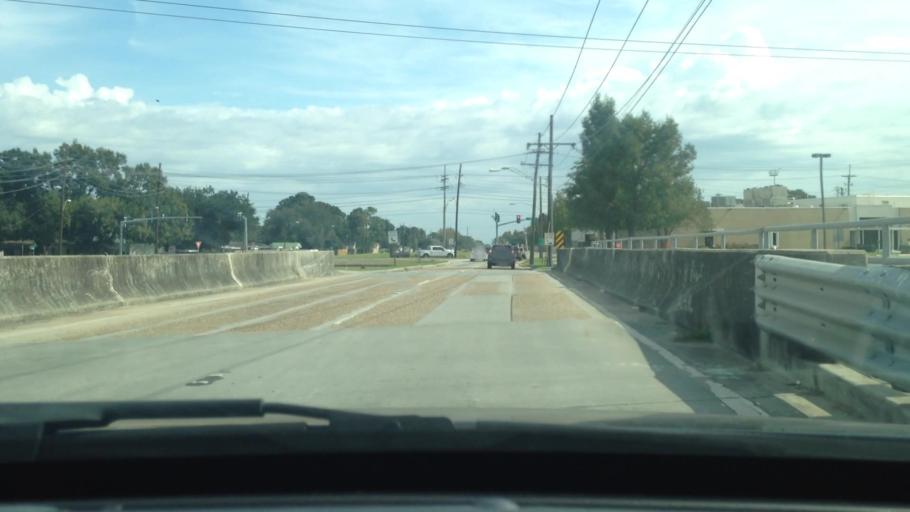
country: US
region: Louisiana
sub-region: Jefferson Parish
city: River Ridge
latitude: 29.9849
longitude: -90.2149
